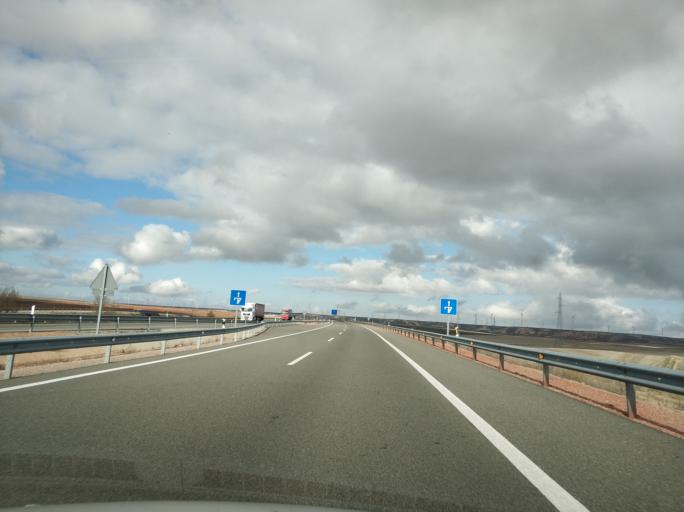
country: ES
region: Castille and Leon
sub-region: Provincia de Soria
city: Alcubilla de las Penas
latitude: 41.2512
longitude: -2.4739
